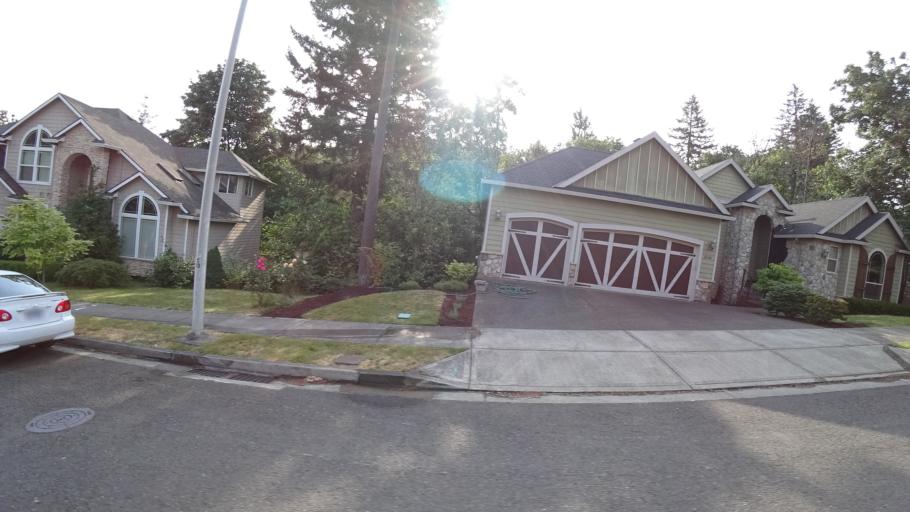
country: US
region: Oregon
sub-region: Clackamas County
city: Happy Valley
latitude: 45.4641
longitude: -122.5262
